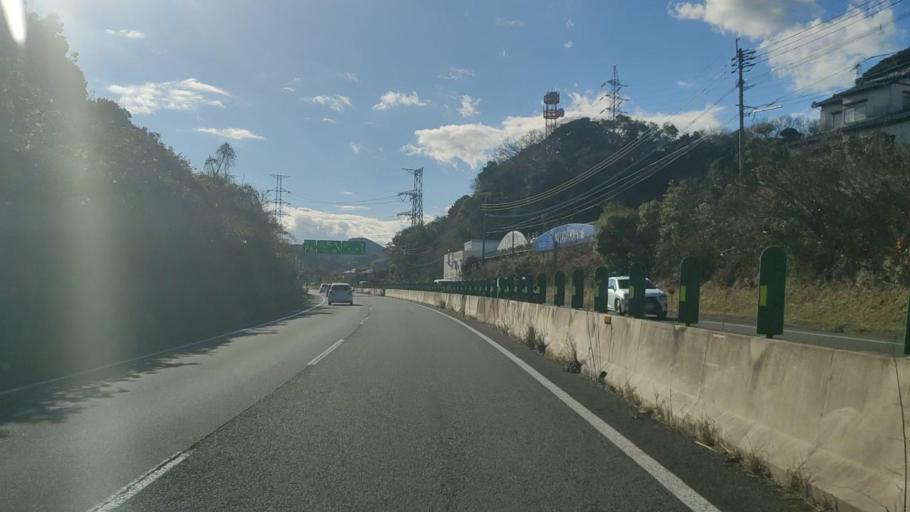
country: JP
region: Fukuoka
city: Kitakyushu
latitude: 33.8627
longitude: 130.8505
